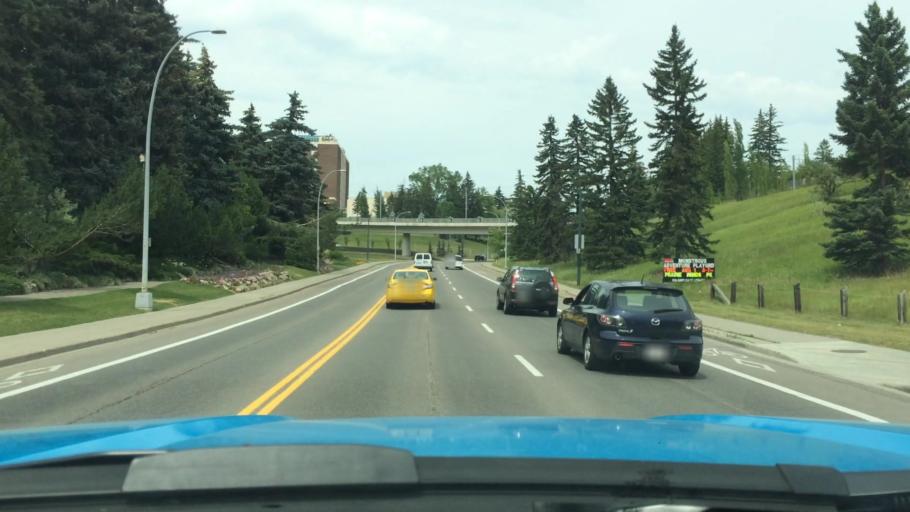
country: CA
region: Alberta
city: Calgary
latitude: 51.0597
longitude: -114.0860
